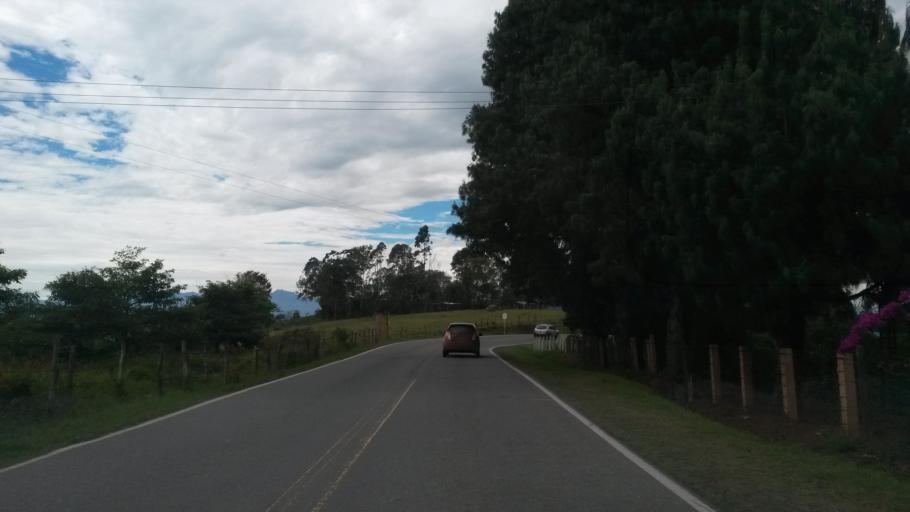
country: CO
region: Cauca
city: Rosas
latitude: 2.3241
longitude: -76.6913
